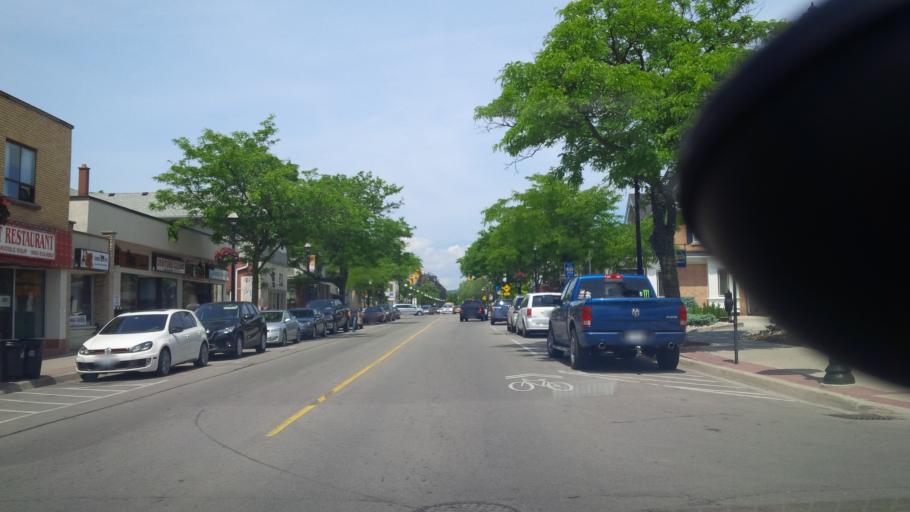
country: CA
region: Ontario
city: Burlington
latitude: 43.3270
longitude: -79.7997
